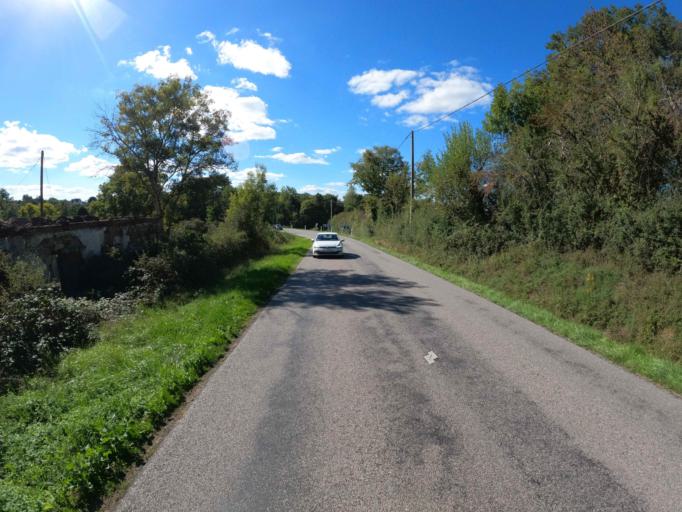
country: FR
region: Auvergne
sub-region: Departement de l'Allier
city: Doyet
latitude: 46.3975
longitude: 2.8722
